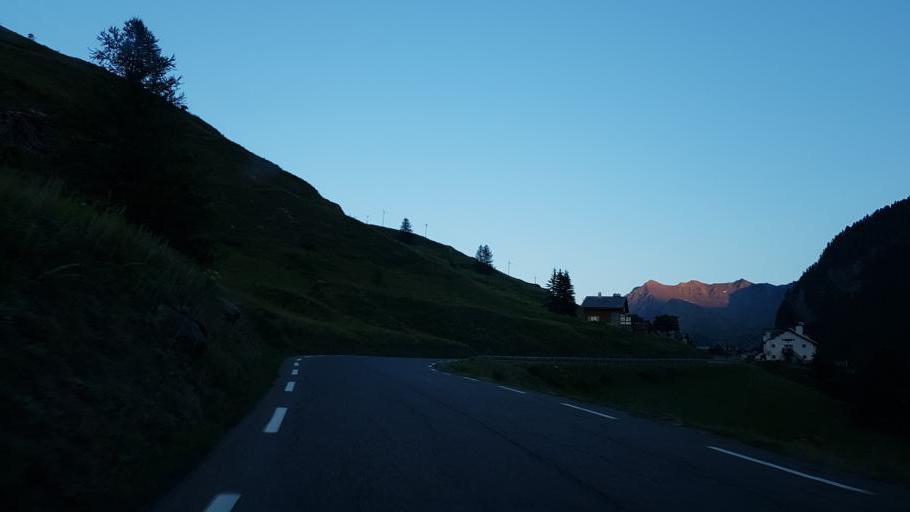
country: IT
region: Piedmont
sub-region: Provincia di Cuneo
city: Pontechianale
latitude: 44.7029
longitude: 6.8572
